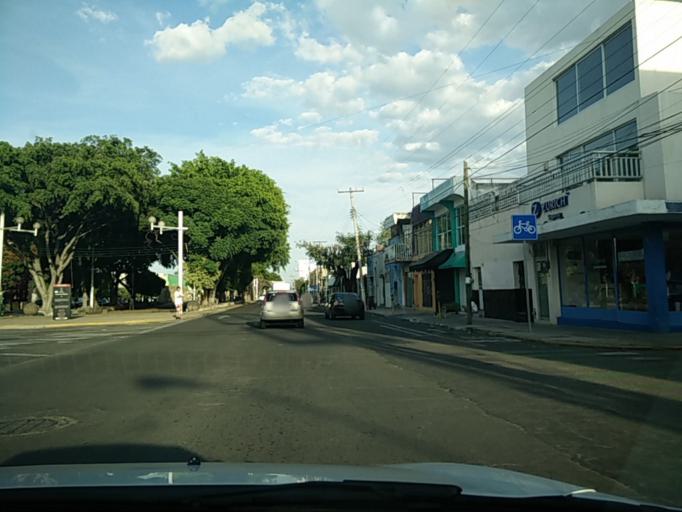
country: MX
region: Jalisco
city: Guadalajara
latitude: 20.6791
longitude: -103.3718
